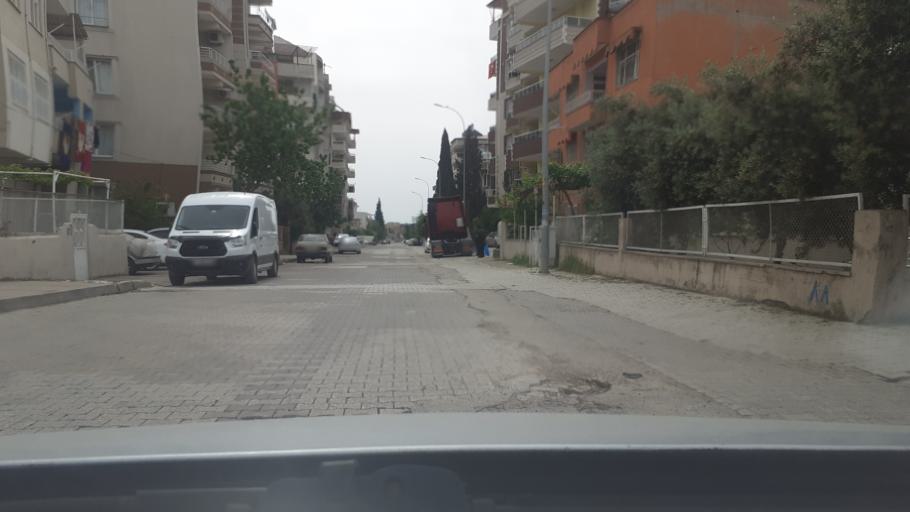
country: TR
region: Hatay
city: Kirikhan
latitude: 36.4957
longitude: 36.3630
